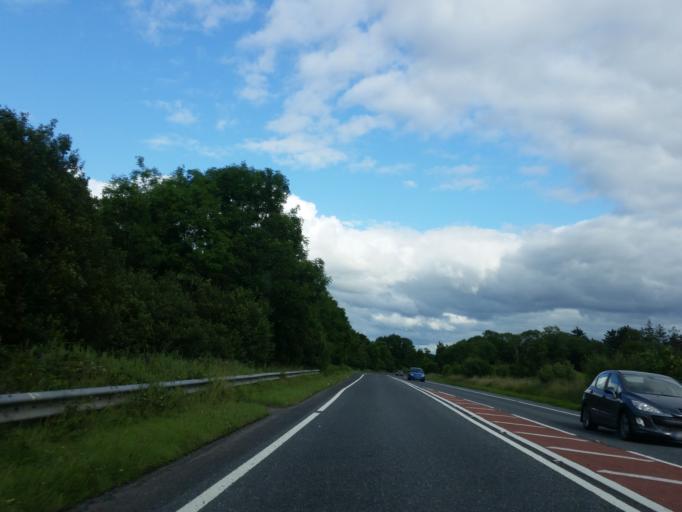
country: GB
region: Northern Ireland
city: Lisnaskea
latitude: 54.3129
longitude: -7.5051
